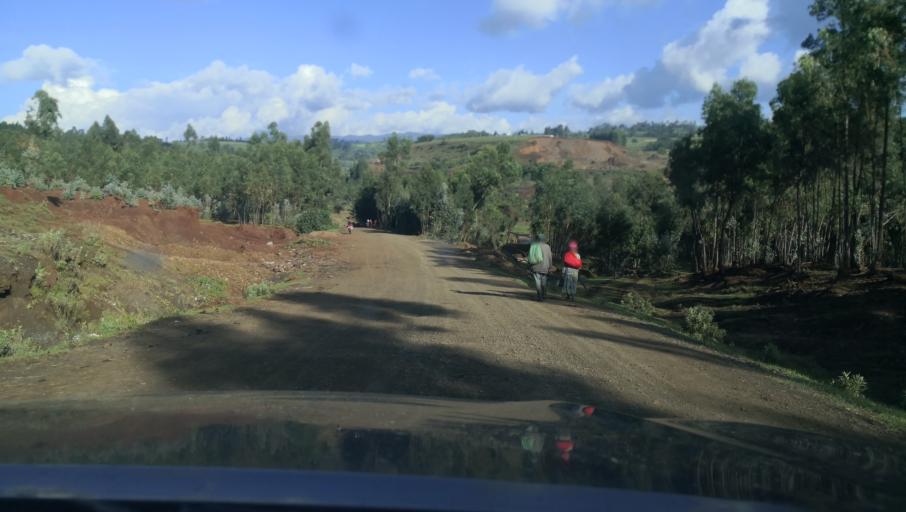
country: ET
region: Oromiya
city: Tulu Bolo
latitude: 8.4568
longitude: 38.2510
